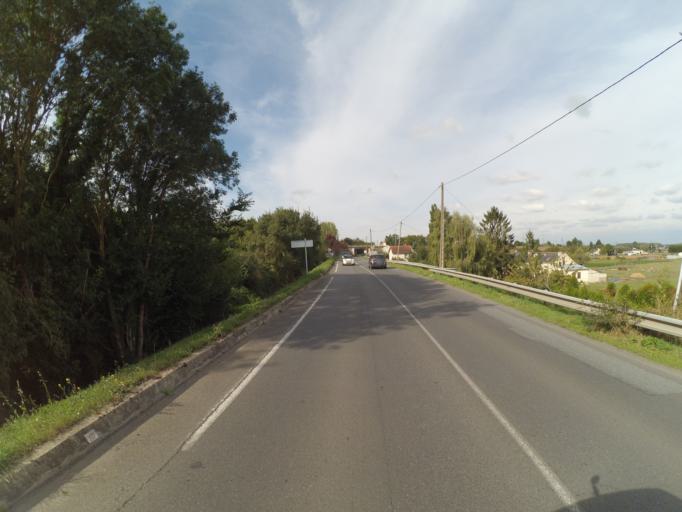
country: FR
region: Pays de la Loire
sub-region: Departement de Maine-et-Loire
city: Villebernier
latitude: 47.2601
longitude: -0.0491
